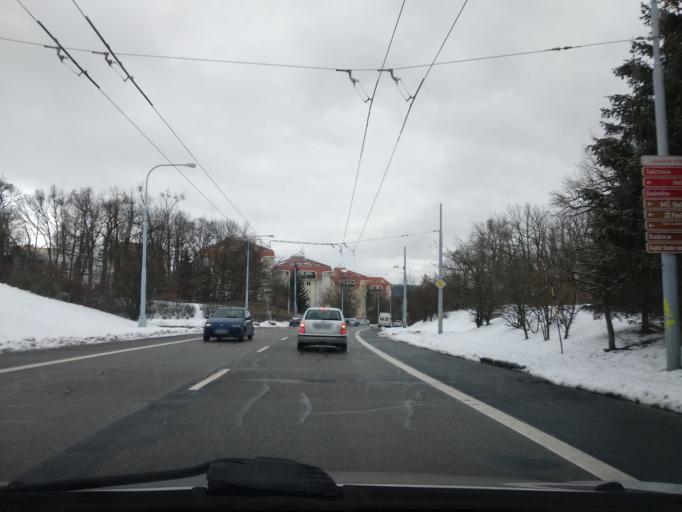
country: CZ
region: South Moravian
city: Troubsko
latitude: 49.1927
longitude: 16.5300
